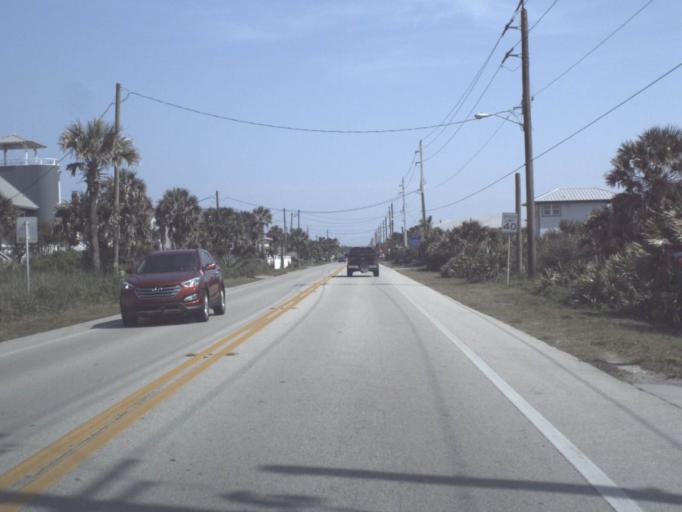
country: US
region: Florida
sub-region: Saint Johns County
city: Villano Beach
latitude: 29.9285
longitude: -81.2963
